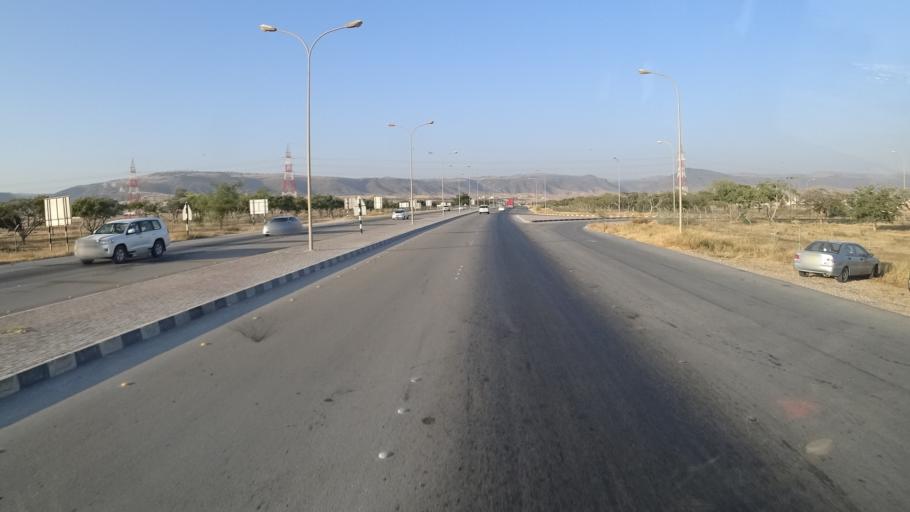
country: OM
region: Zufar
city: Salalah
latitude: 17.1001
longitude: 54.1489
